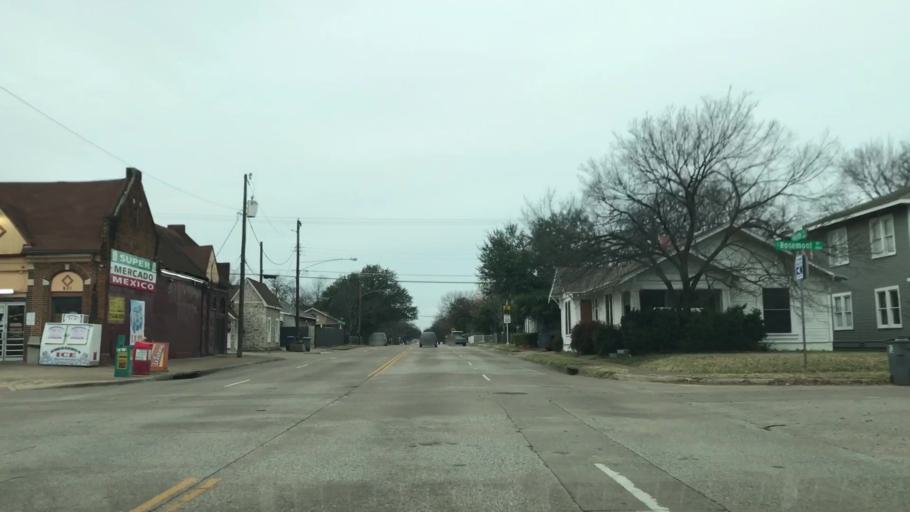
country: US
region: Texas
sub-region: Dallas County
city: Cockrell Hill
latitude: 32.7414
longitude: -96.8477
